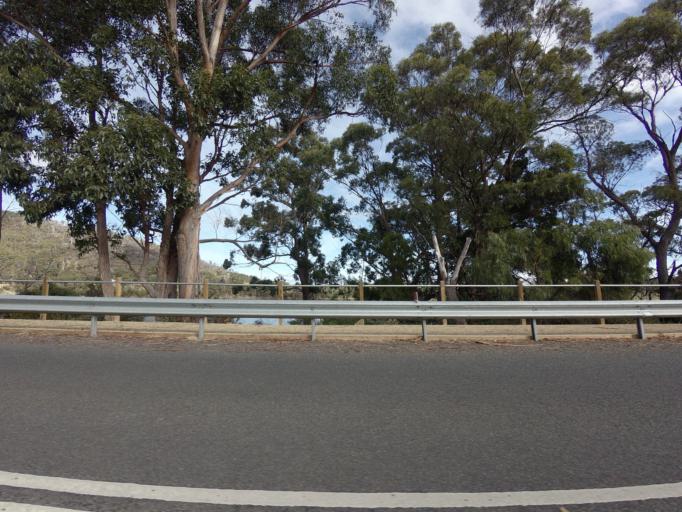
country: AU
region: Tasmania
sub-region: Clarence
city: Sandford
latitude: -43.1071
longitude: 147.7447
